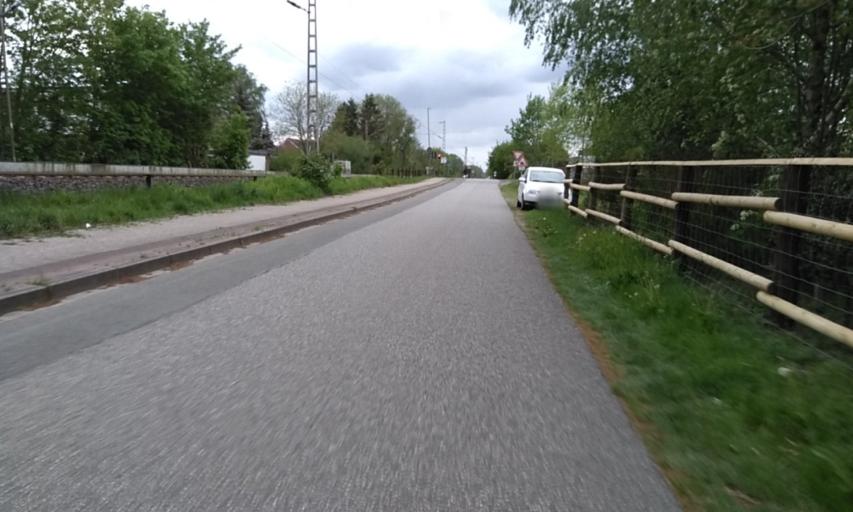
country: DE
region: Lower Saxony
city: Nottensdorf
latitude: 53.4842
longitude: 9.6327
